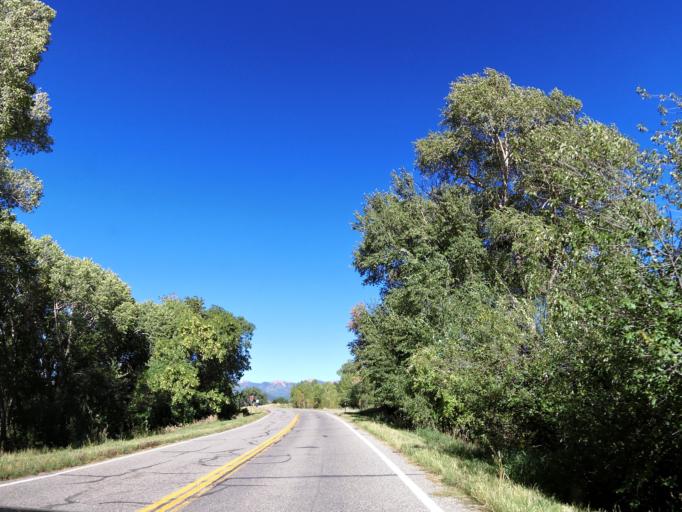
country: US
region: Colorado
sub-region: Montezuma County
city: Mancos
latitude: 37.3444
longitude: -108.2824
